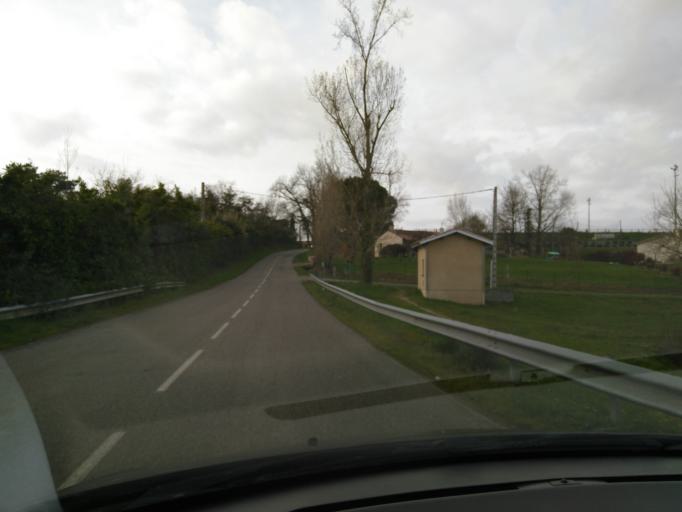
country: FR
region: Midi-Pyrenees
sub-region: Departement du Tarn-et-Garonne
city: Finhan
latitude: 43.8952
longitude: 1.1372
